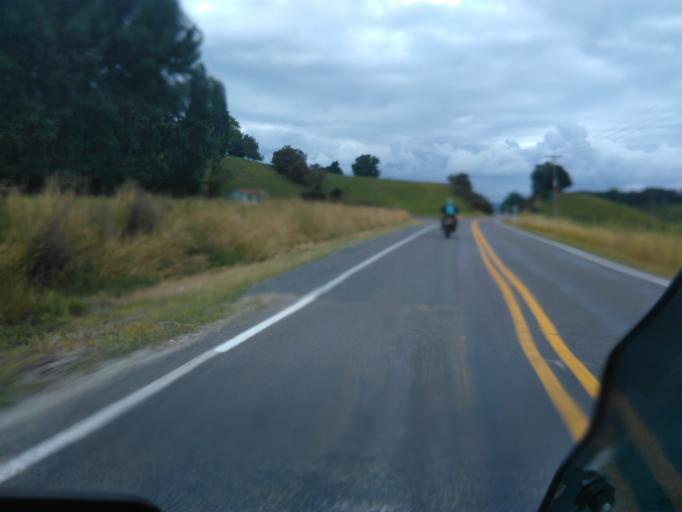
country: NZ
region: Gisborne
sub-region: Gisborne District
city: Gisborne
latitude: -38.4548
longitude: 177.7712
